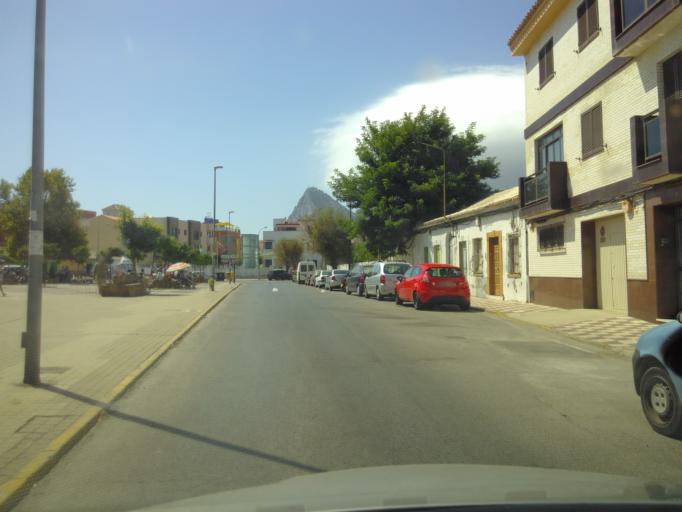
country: ES
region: Andalusia
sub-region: Provincia de Cadiz
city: La Linea de la Concepcion
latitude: 36.1678
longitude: -5.3477
